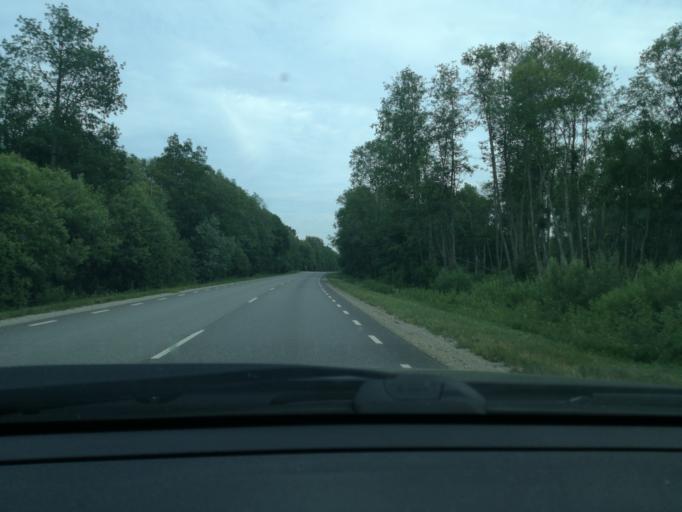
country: EE
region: Laeaene
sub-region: Lihula vald
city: Lihula
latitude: 58.5909
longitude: 23.7134
